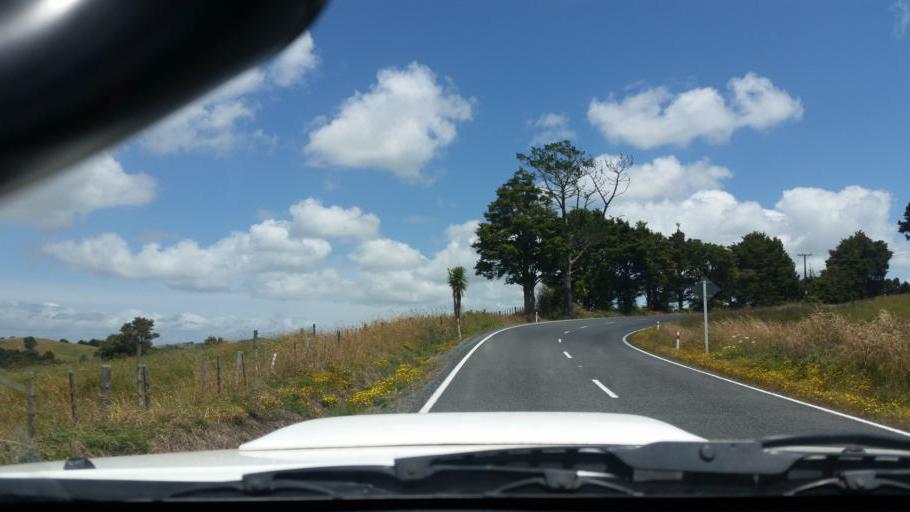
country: NZ
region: Northland
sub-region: Whangarei
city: Ruakaka
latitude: -36.0455
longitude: 174.2784
